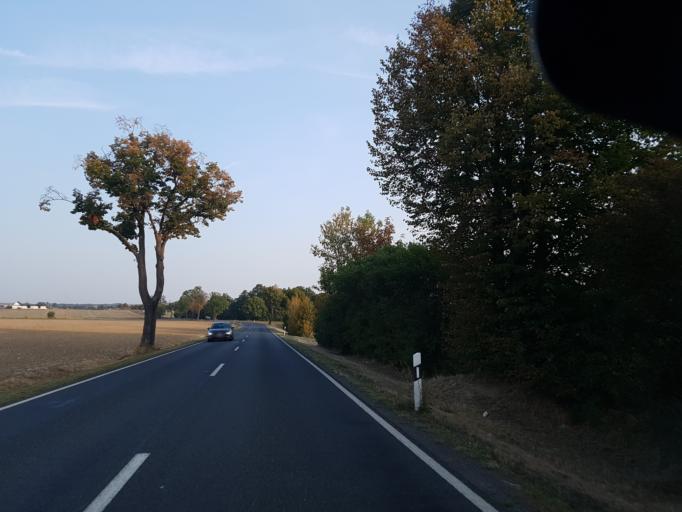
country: DE
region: Saxony
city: Elsnig
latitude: 51.6002
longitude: 12.9417
